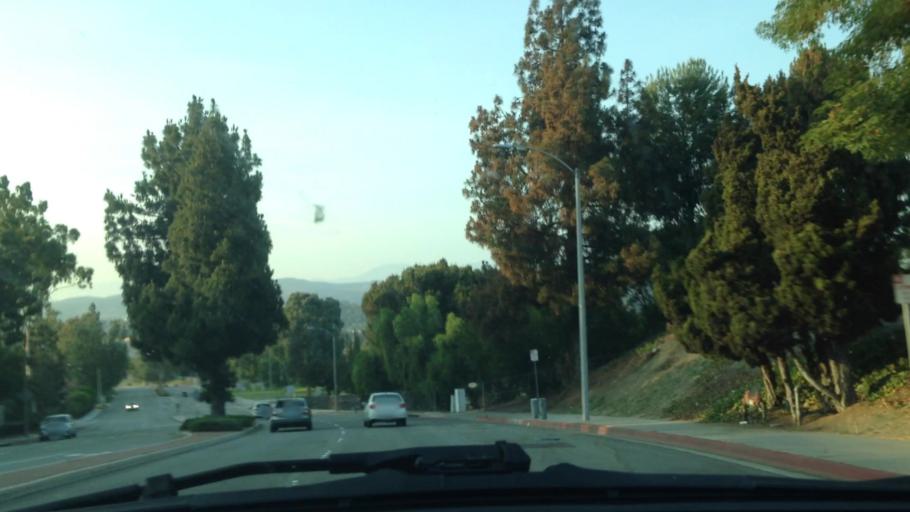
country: US
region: California
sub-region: Orange County
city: Villa Park
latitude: 33.8450
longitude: -117.7903
